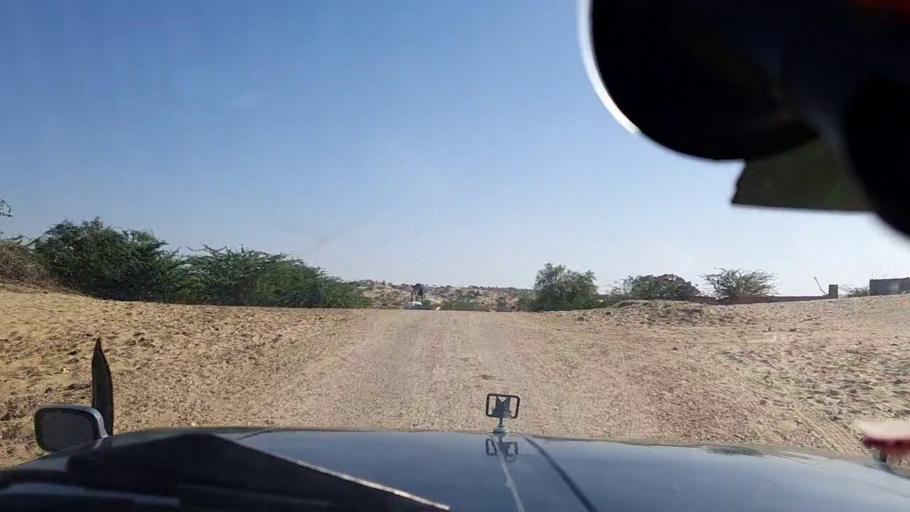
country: PK
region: Sindh
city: Diplo
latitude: 24.4707
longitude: 69.7943
